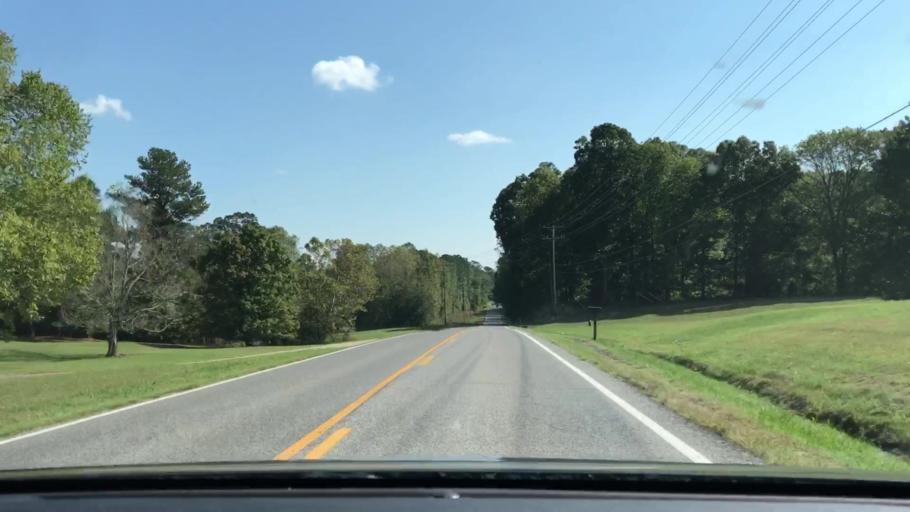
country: US
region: Kentucky
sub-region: Marshall County
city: Benton
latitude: 36.7645
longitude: -88.2518
